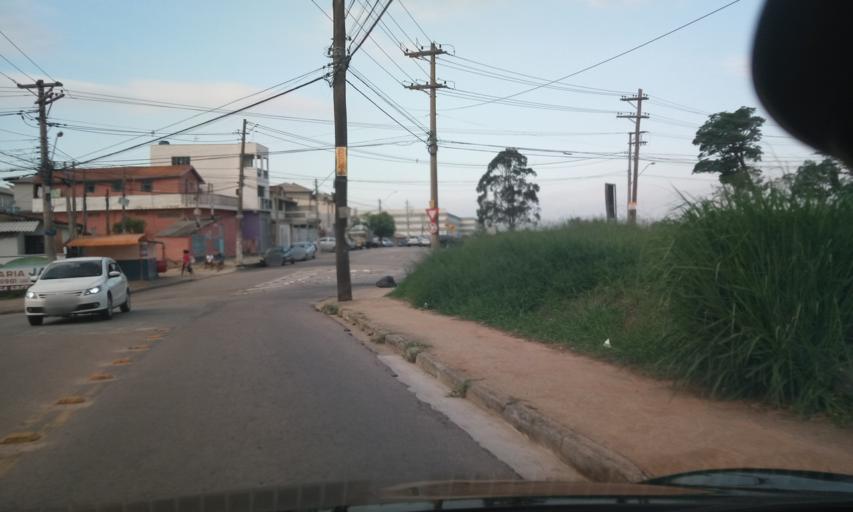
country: BR
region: Sao Paulo
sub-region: Itupeva
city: Itupeva
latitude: -23.1781
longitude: -46.9847
